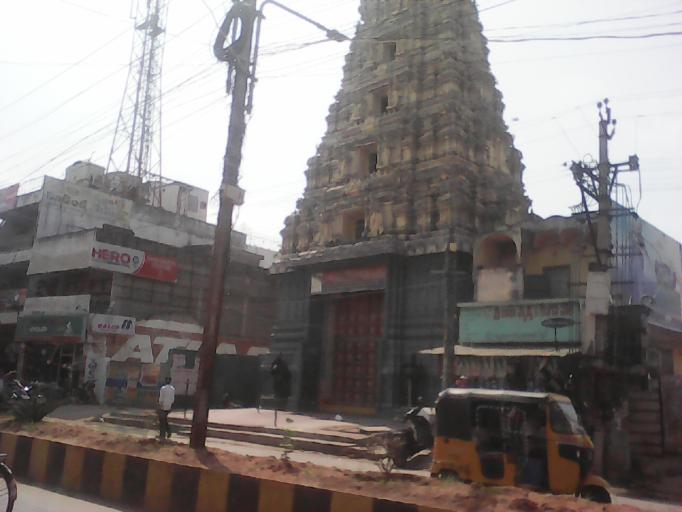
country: IN
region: Andhra Pradesh
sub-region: Guntur
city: Bhattiprolu
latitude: 16.2364
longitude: 80.6498
